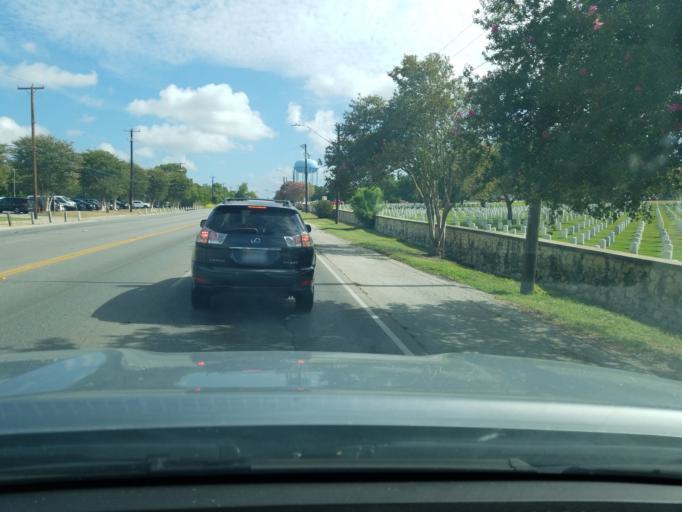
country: US
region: Texas
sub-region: Bexar County
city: Terrell Hills
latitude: 29.4754
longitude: -98.4352
